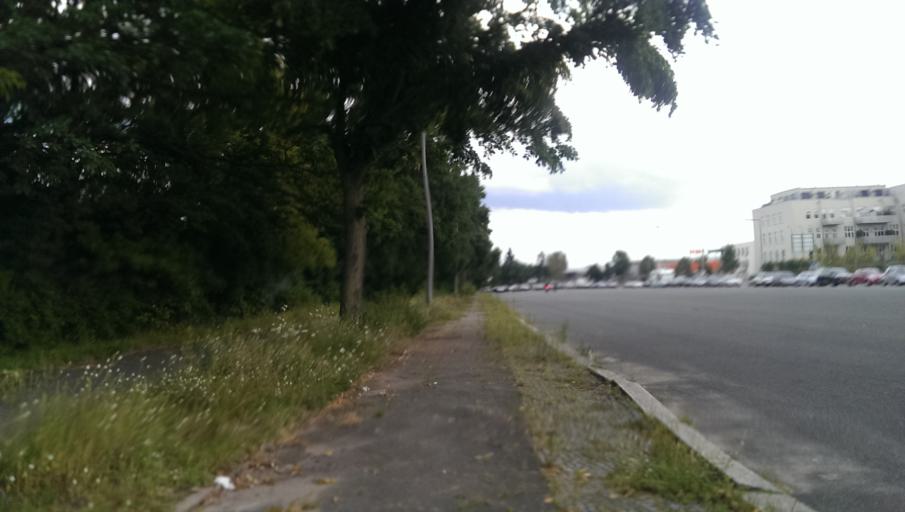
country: DE
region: Berlin
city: Lichterfelde
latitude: 52.4206
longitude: 13.2885
